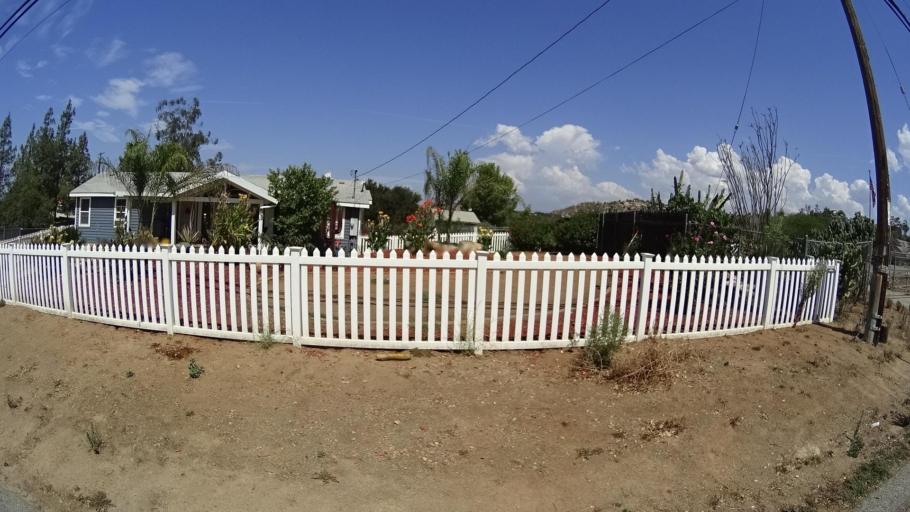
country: US
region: California
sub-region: San Diego County
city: Valley Center
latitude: 33.2261
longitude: -117.0693
